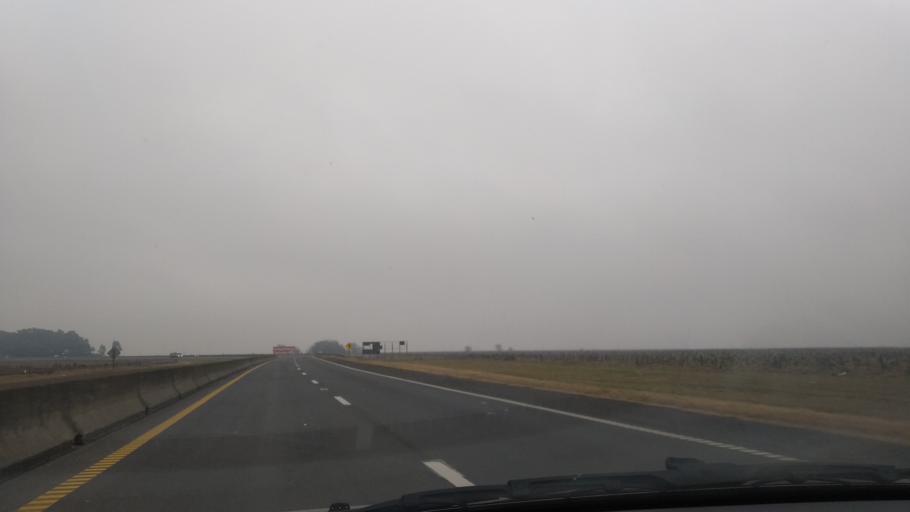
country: AR
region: Buenos Aires
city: Olavarria
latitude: -36.8550
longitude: -60.1006
